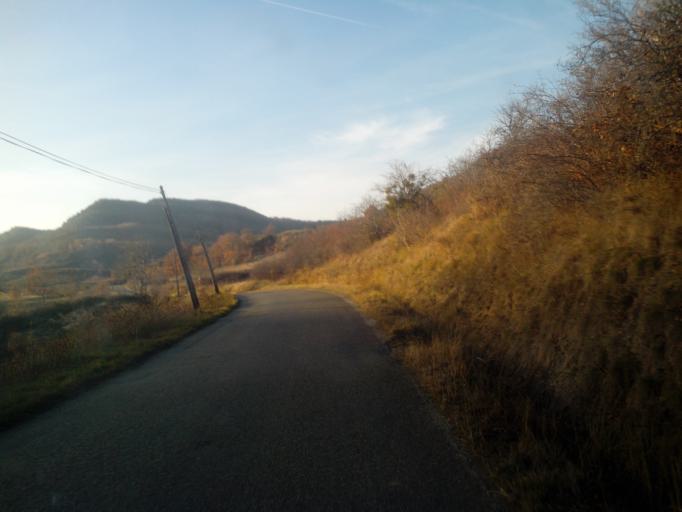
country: FR
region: Languedoc-Roussillon
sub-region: Departement de l'Aude
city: Esperaza
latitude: 42.9419
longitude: 2.1844
